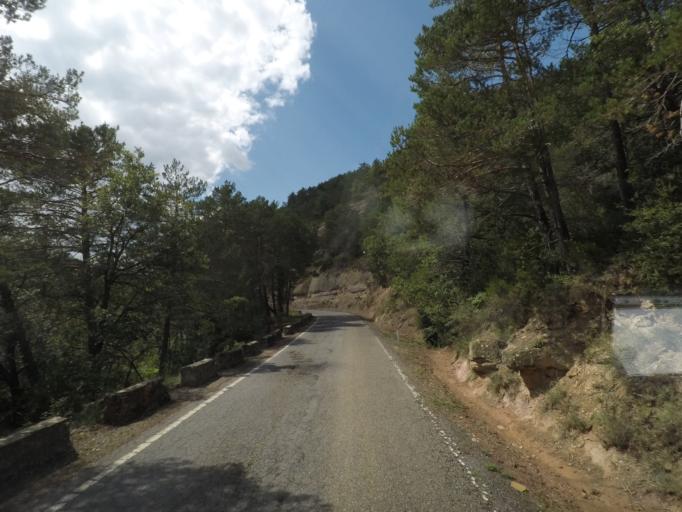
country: ES
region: Aragon
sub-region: Provincia de Huesca
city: Yebra de Basa
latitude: 42.4053
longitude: -0.2358
